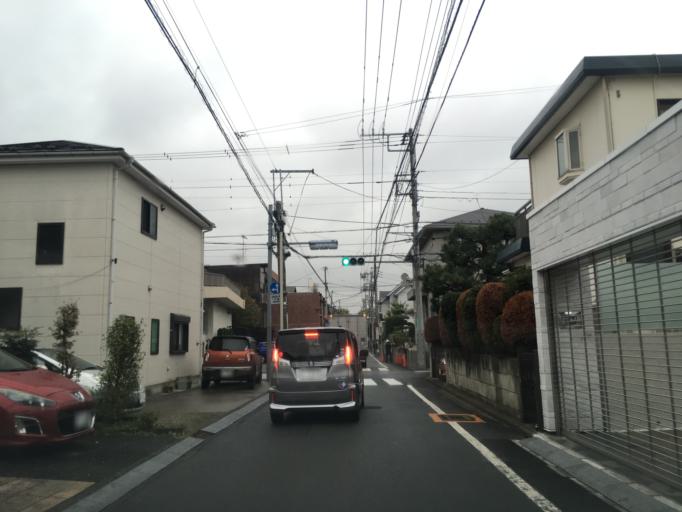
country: JP
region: Tokyo
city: Kokubunji
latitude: 35.6976
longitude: 139.4410
